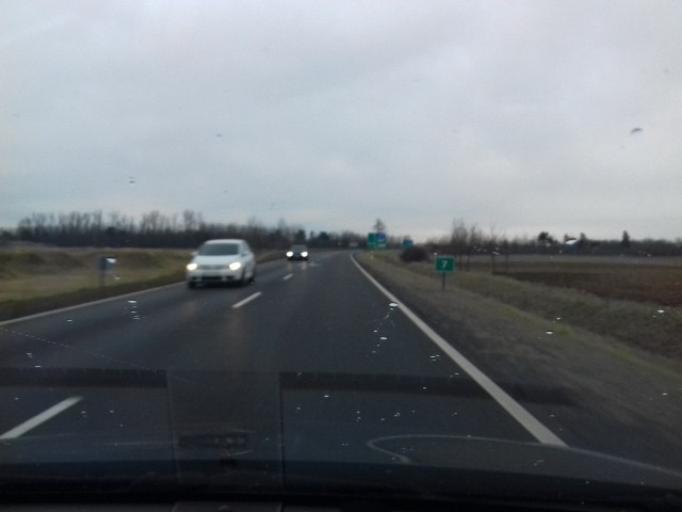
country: HU
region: Szabolcs-Szatmar-Bereg
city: Nyirpazony
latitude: 47.9555
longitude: 21.8191
